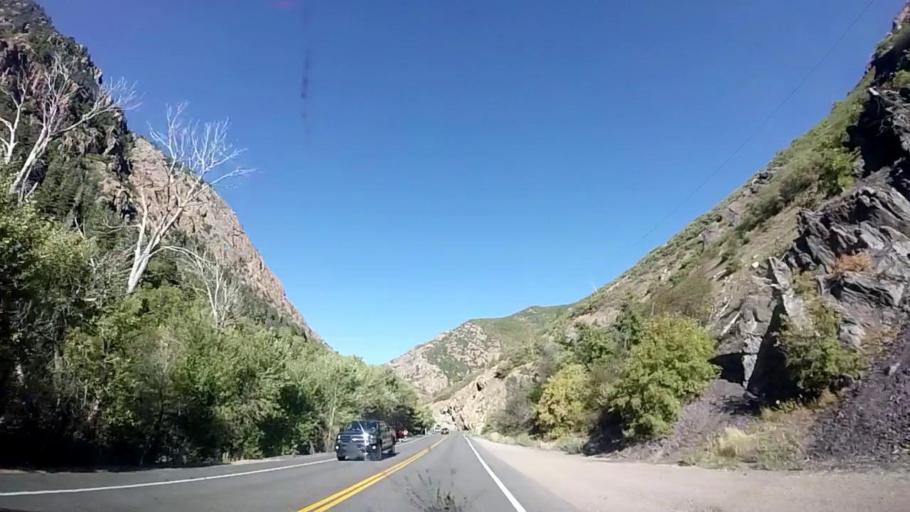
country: US
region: Utah
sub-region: Salt Lake County
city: Cottonwood Heights
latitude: 40.6231
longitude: -111.7569
